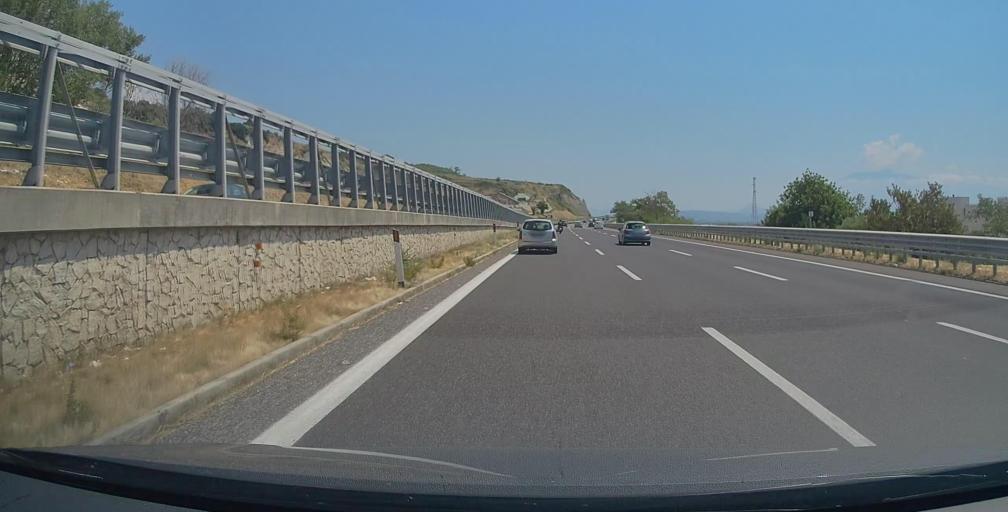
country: IT
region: Campania
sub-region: Provincia di Salerno
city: Battipaglia
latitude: 40.6029
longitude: 15.0229
